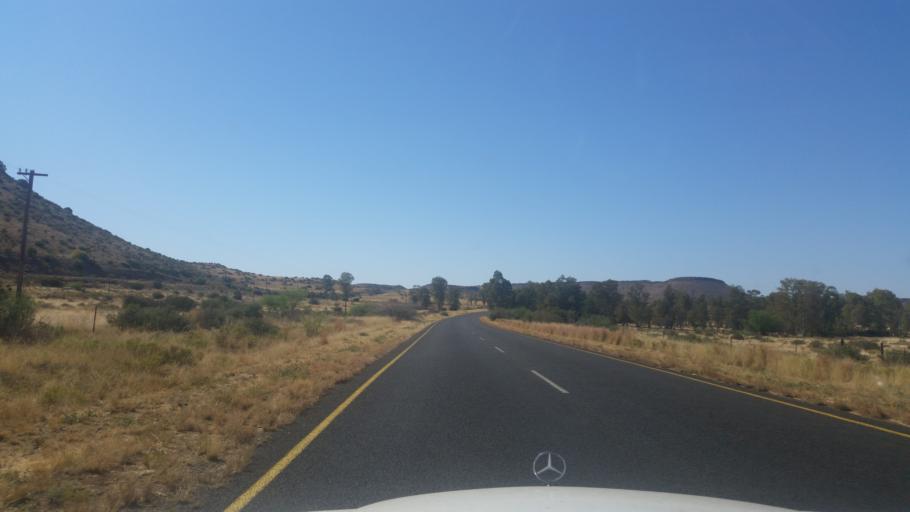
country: ZA
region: Orange Free State
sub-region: Xhariep District Municipality
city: Trompsburg
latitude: -30.4966
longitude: 26.0023
